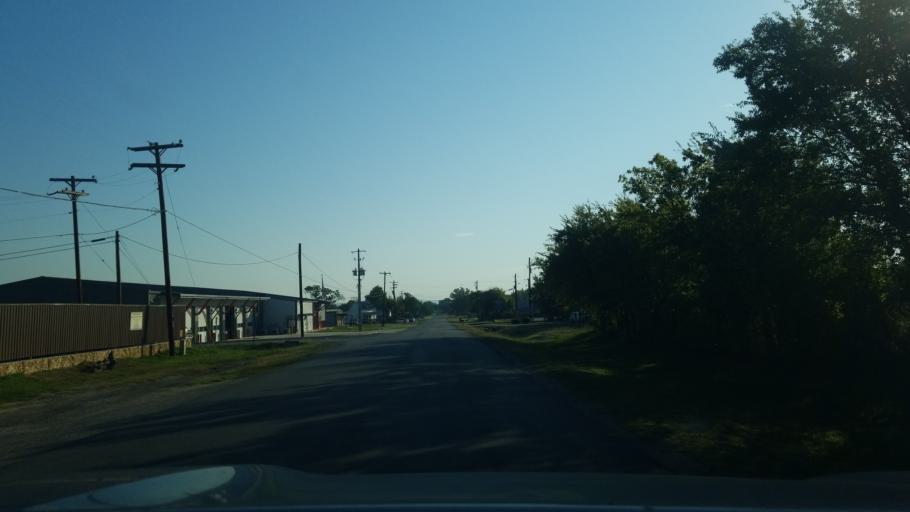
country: US
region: Texas
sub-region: Blanco County
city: Blanco
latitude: 30.0887
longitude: -98.4182
